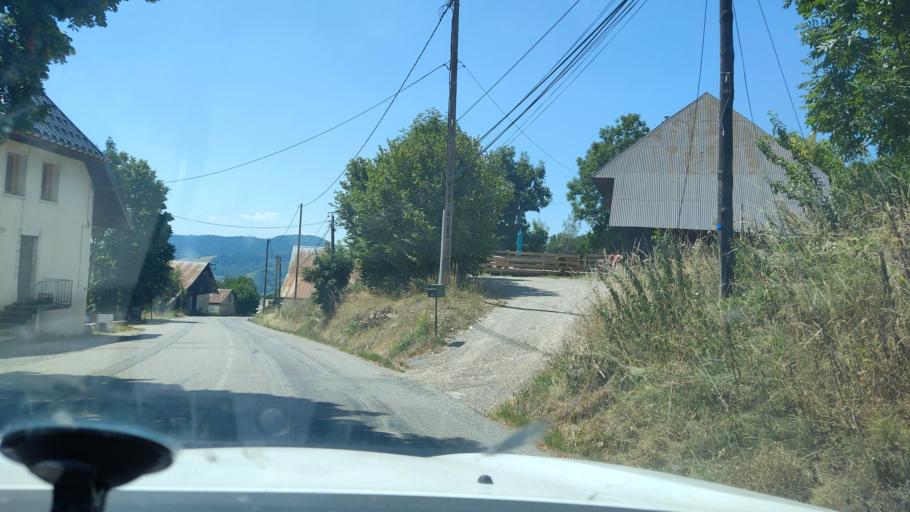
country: FR
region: Rhone-Alpes
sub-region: Departement de la Savoie
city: Mery
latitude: 45.6440
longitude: 6.0147
